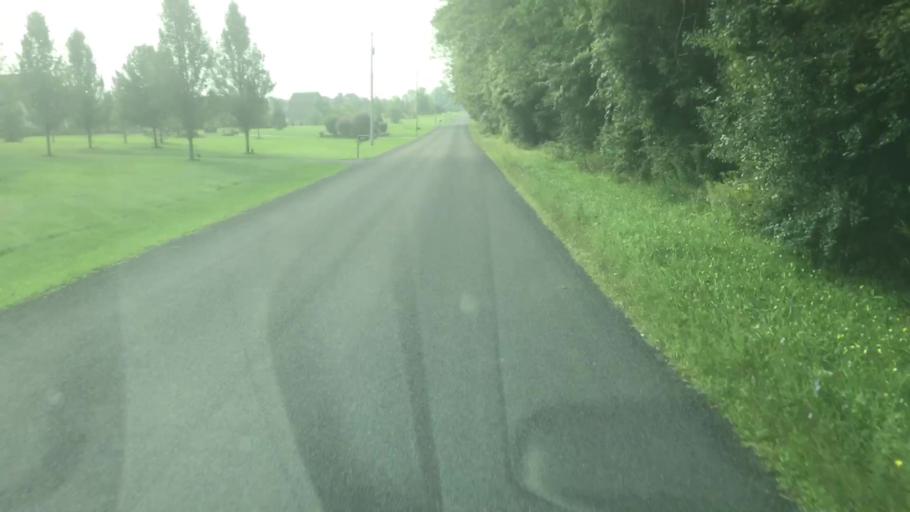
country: US
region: New York
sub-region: Onondaga County
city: Skaneateles
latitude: 42.9120
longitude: -76.4555
